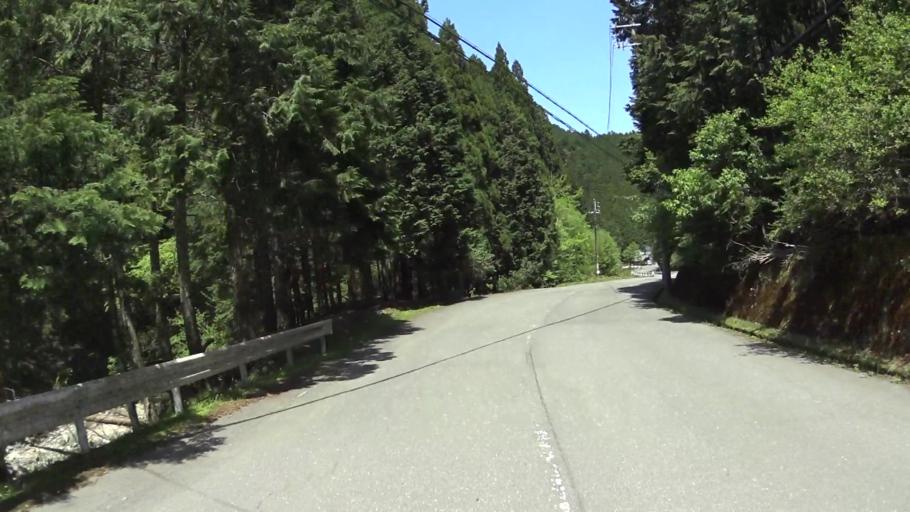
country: JP
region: Shiga Prefecture
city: Kitahama
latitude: 35.1944
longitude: 135.7858
